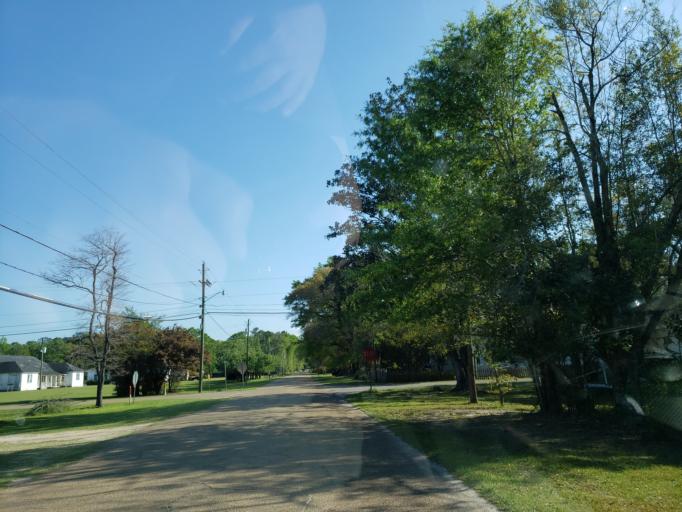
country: US
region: Mississippi
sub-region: Perry County
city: New Augusta
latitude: 31.1680
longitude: -88.9209
